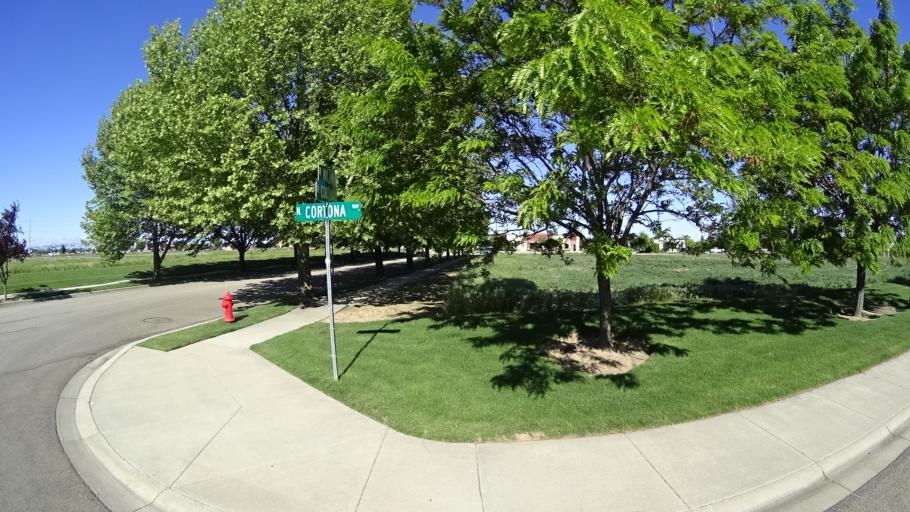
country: US
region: Idaho
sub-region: Ada County
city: Meridian
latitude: 43.6510
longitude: -116.4310
